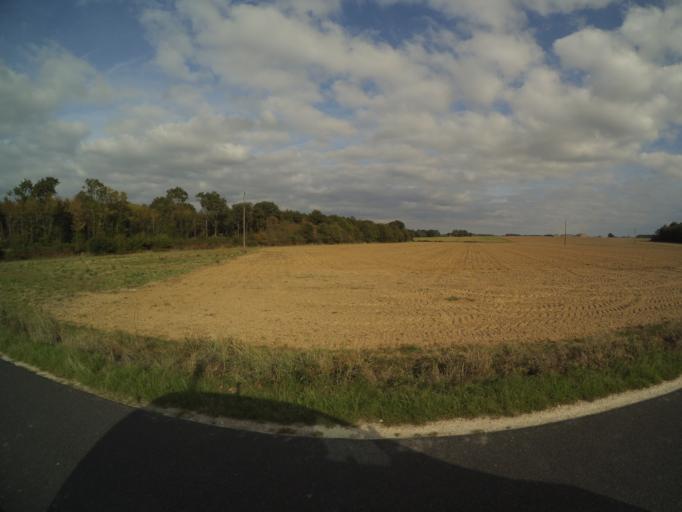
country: FR
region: Centre
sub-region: Departement d'Indre-et-Loire
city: Nazelles-Negron
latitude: 47.4682
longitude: 0.9550
